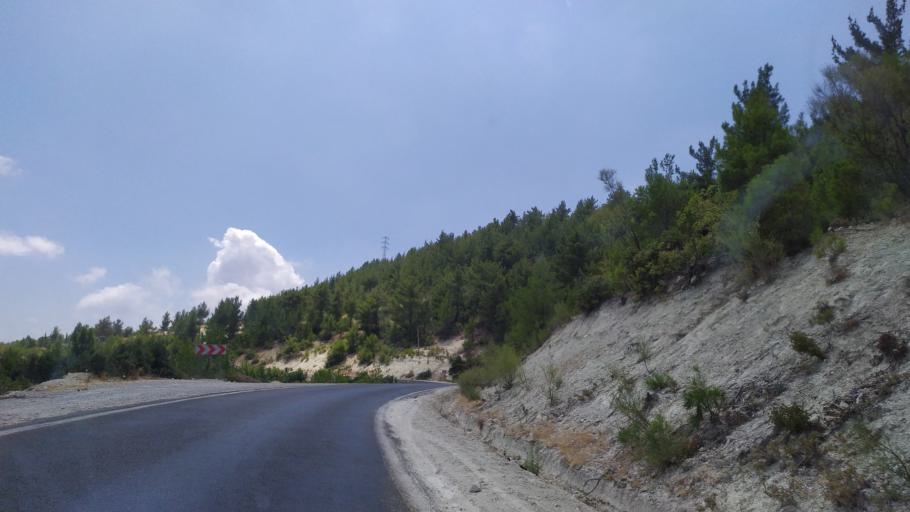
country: TR
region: Mersin
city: Gulnar
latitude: 36.2922
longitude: 33.3803
